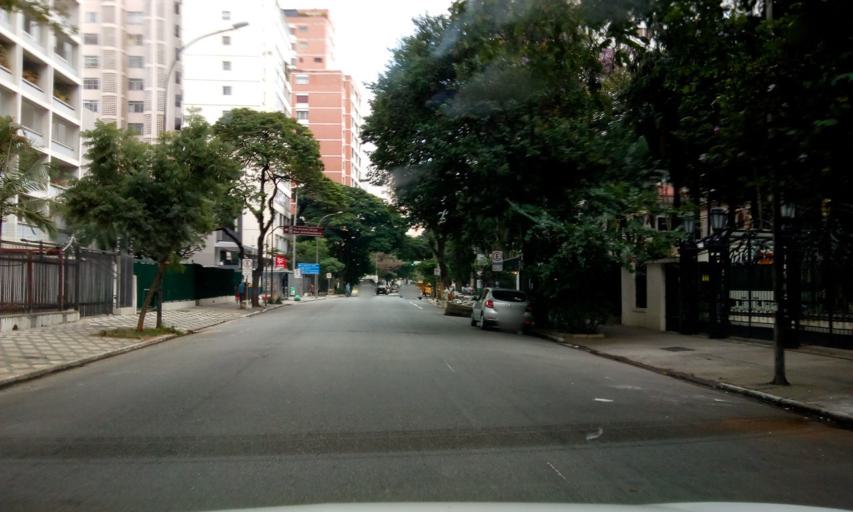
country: BR
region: Sao Paulo
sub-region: Sao Paulo
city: Sao Paulo
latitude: -23.5441
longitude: -46.6553
